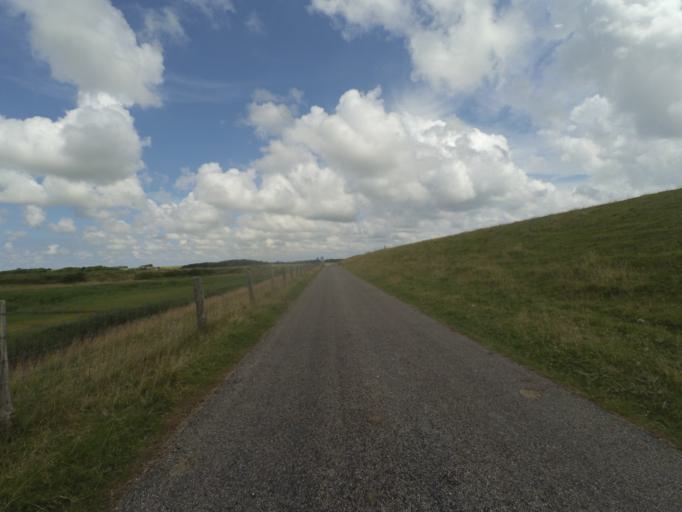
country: NL
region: North Holland
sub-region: Gemeente Texel
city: Den Burg
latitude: 53.0287
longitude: 4.8177
